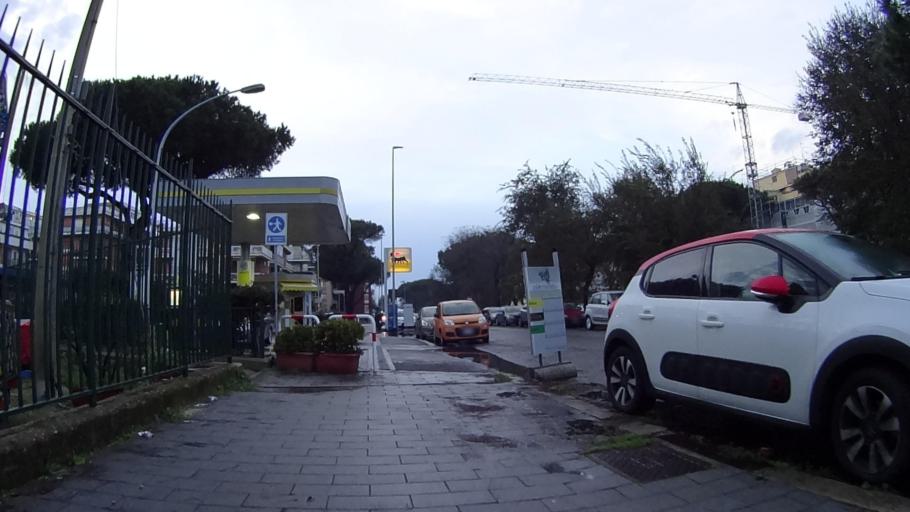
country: IT
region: Latium
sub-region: Citta metropolitana di Roma Capitale
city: Lido di Ostia
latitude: 41.7354
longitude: 12.2879
